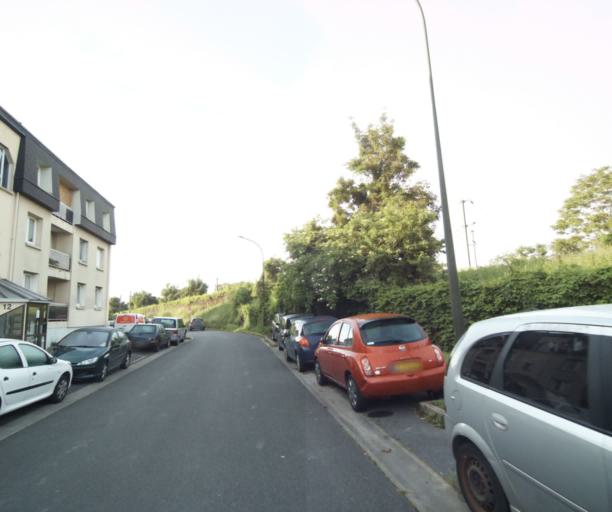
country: FR
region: Ile-de-France
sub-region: Departement du Val-d'Oise
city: Argenteuil
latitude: 48.9513
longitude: 2.2559
